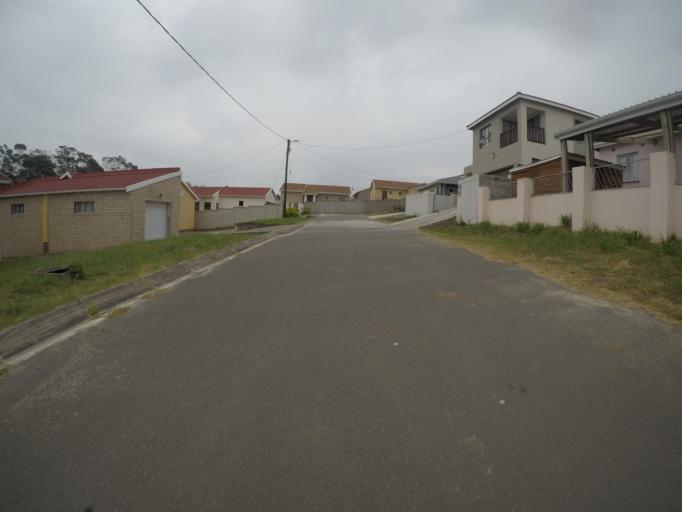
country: ZA
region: Eastern Cape
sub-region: Buffalo City Metropolitan Municipality
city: East London
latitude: -32.9939
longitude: 27.8437
